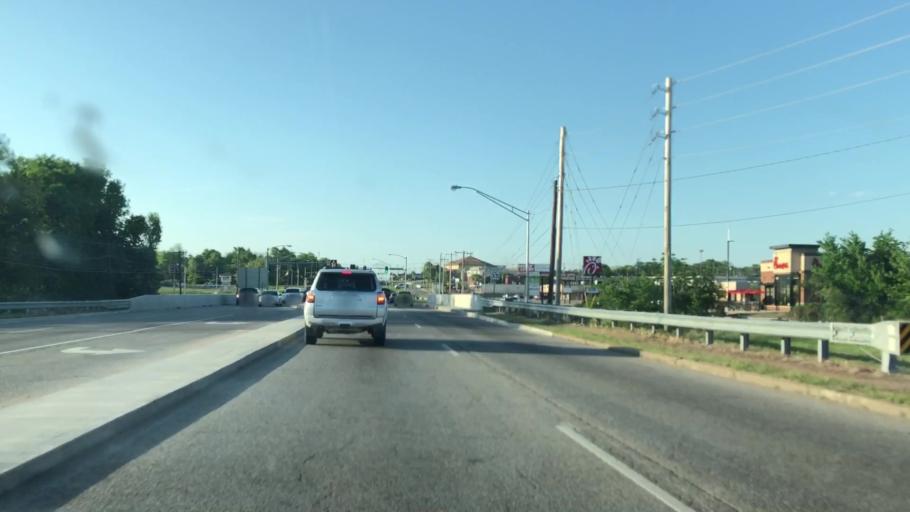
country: US
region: Oklahoma
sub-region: Washington County
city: Bartlesville
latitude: 36.7470
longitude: -95.9353
